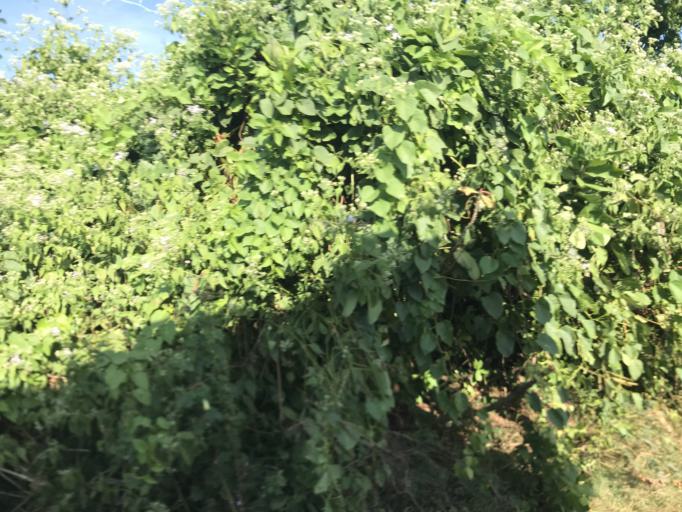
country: IN
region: Karnataka
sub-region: Mysore
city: Sargur
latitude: 11.9451
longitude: 76.2657
